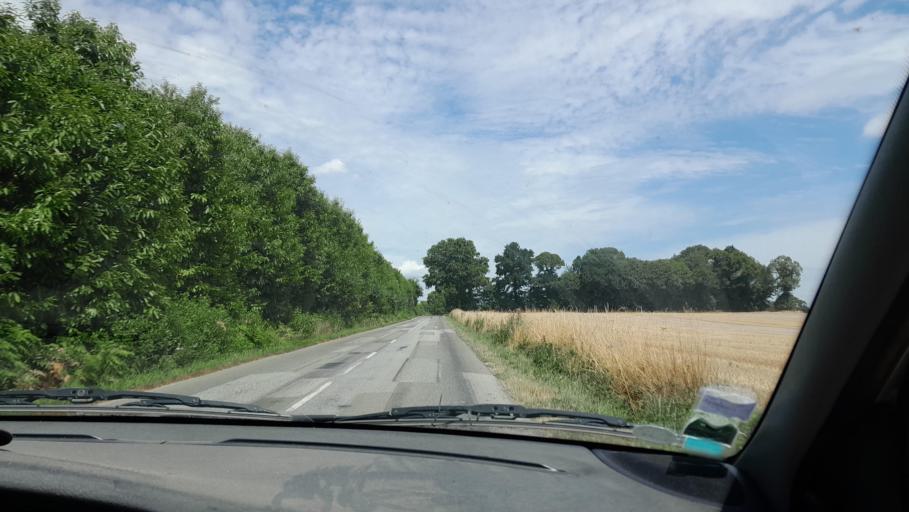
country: FR
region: Brittany
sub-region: Departement d'Ille-et-Vilaine
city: Le Pertre
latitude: 48.0549
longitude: -1.0328
